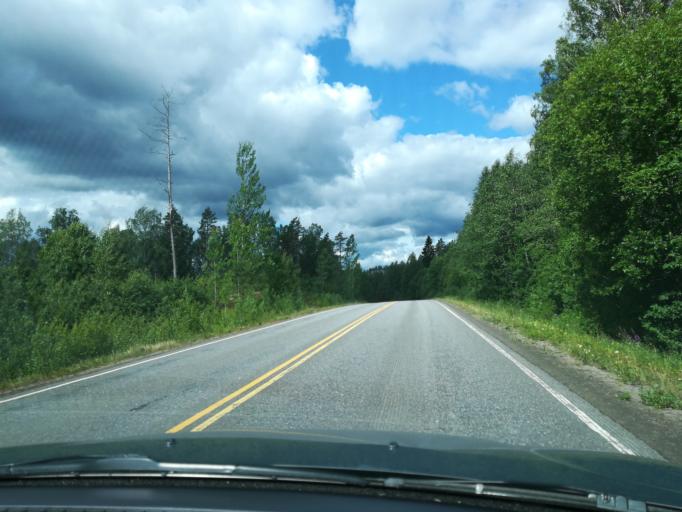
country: FI
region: Southern Savonia
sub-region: Mikkeli
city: Maentyharju
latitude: 61.3660
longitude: 26.9384
